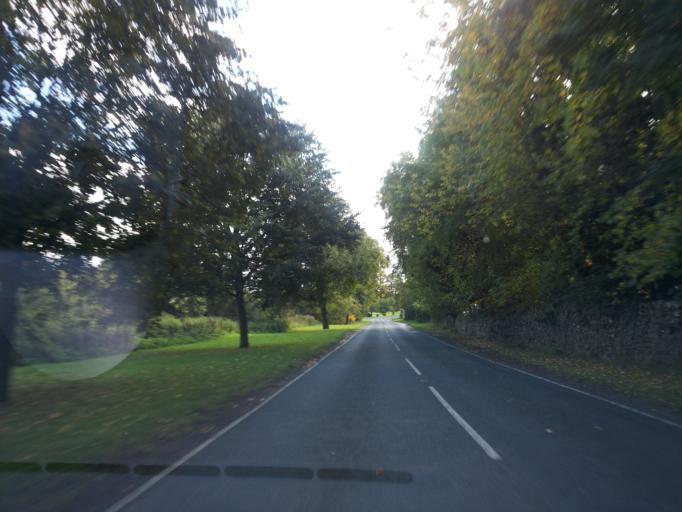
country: GB
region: England
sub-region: North Yorkshire
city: Leyburn
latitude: 54.2908
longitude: -1.8125
